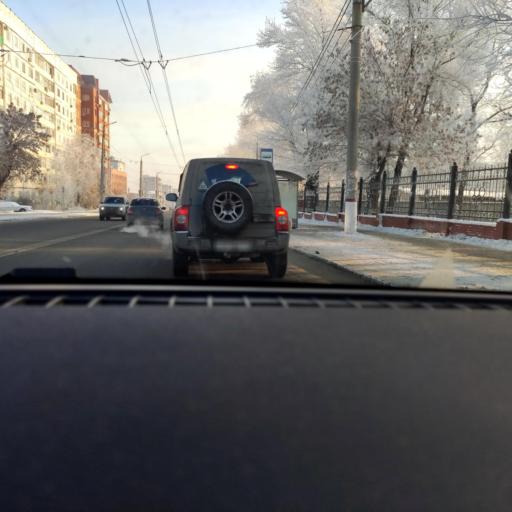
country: RU
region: Samara
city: Novokuybyshevsk
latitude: 53.0944
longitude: 49.9758
